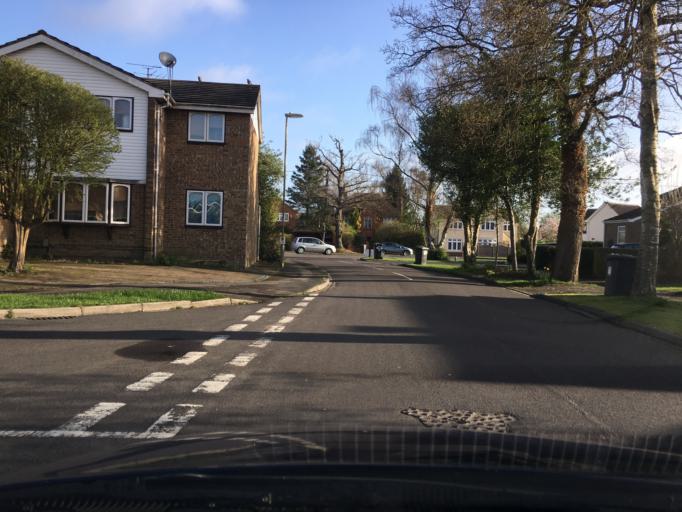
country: GB
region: England
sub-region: Bracknell Forest
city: Sandhurst
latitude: 51.3359
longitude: -0.7983
